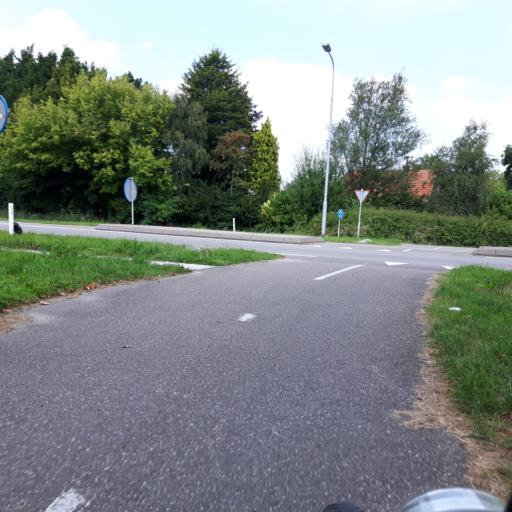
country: NL
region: Zeeland
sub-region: Gemeente Goes
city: Goes
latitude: 51.4910
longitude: 3.9613
